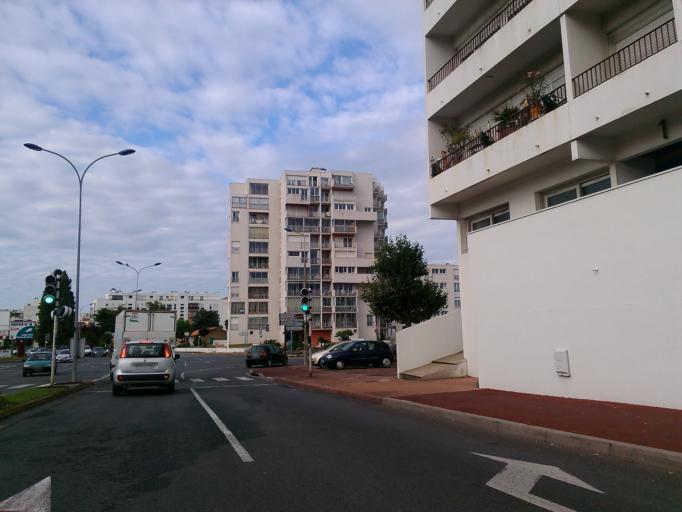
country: FR
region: Poitou-Charentes
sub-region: Departement de la Charente-Maritime
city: Royan
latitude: 45.6322
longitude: -1.0315
